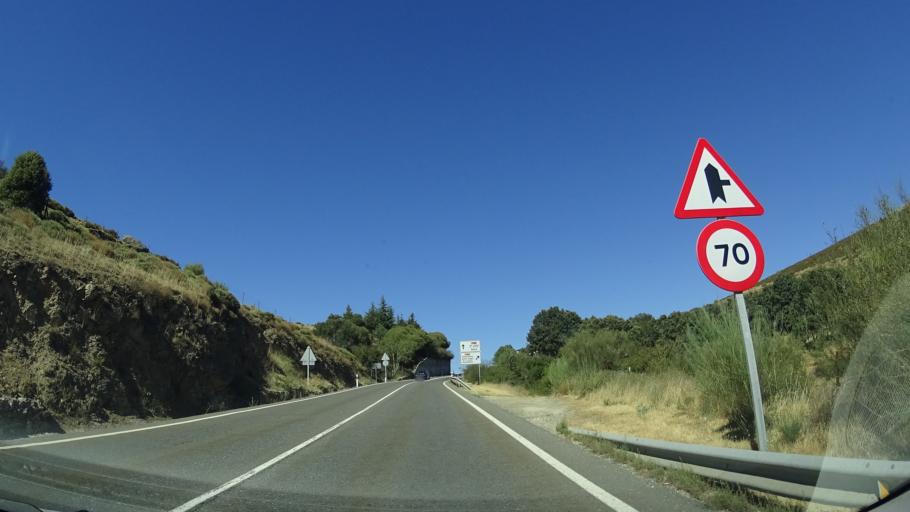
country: ES
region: Madrid
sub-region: Provincia de Madrid
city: Zarzalejo
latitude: 40.5664
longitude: -4.2045
